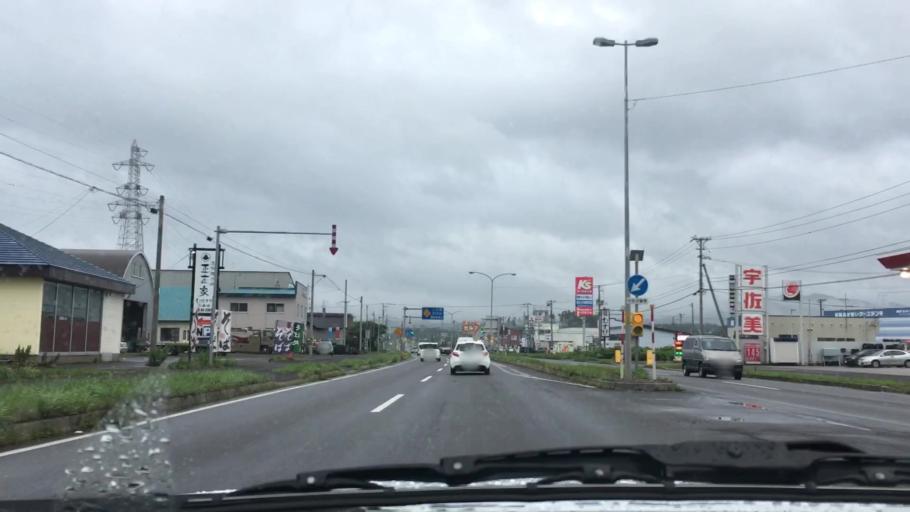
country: JP
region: Hokkaido
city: Nanae
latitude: 42.2506
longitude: 140.2856
